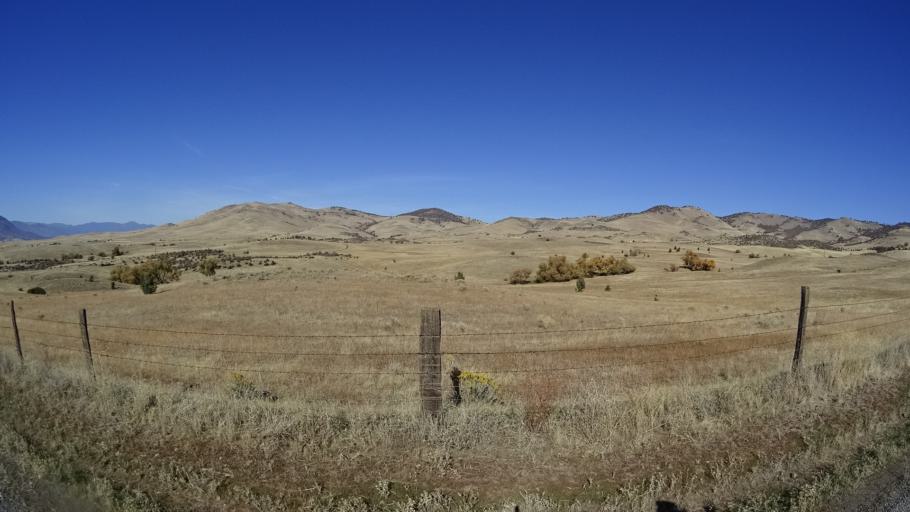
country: US
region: California
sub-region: Siskiyou County
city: Montague
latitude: 41.8149
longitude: -122.3684
